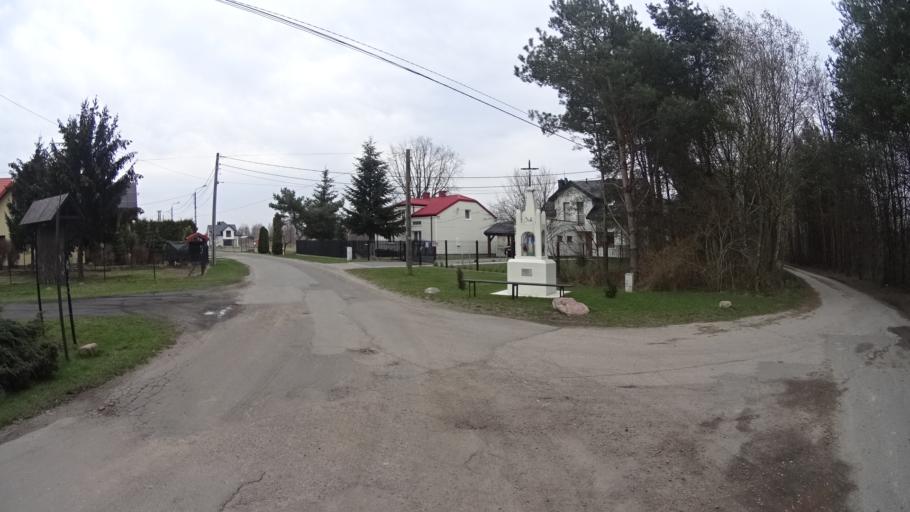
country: PL
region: Masovian Voivodeship
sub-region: Powiat warszawski zachodni
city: Jozefow
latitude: 52.2466
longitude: 20.6724
